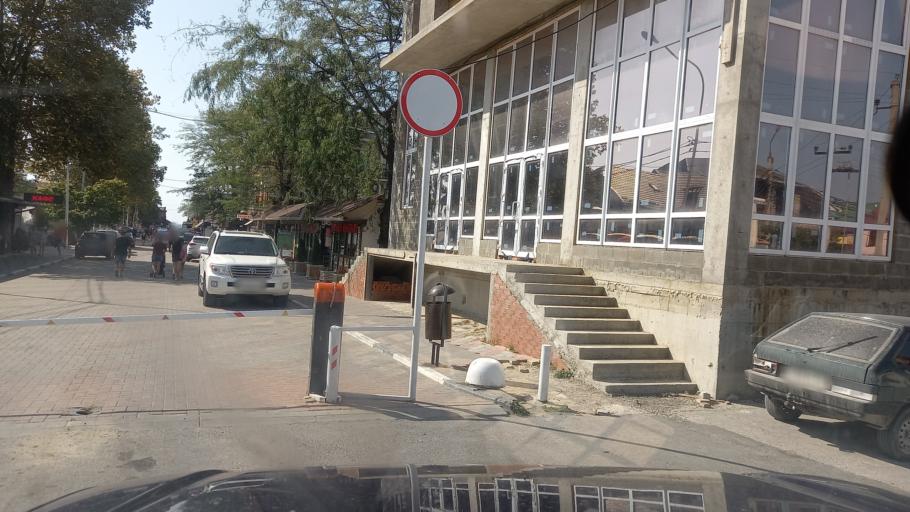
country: RU
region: Krasnodarskiy
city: Arkhipo-Osipovka
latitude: 44.3607
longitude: 38.5321
